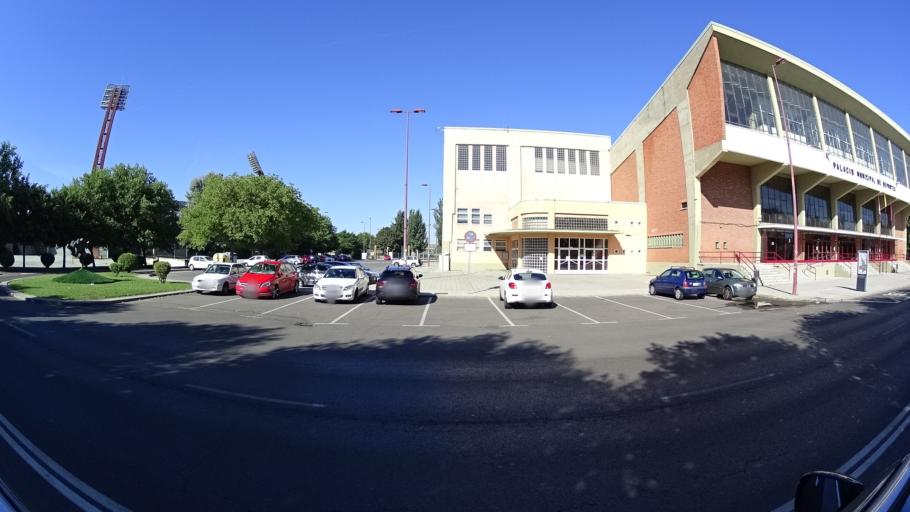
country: ES
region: Castille and Leon
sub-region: Provincia de Leon
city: Leon
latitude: 42.5890
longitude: -5.5764
